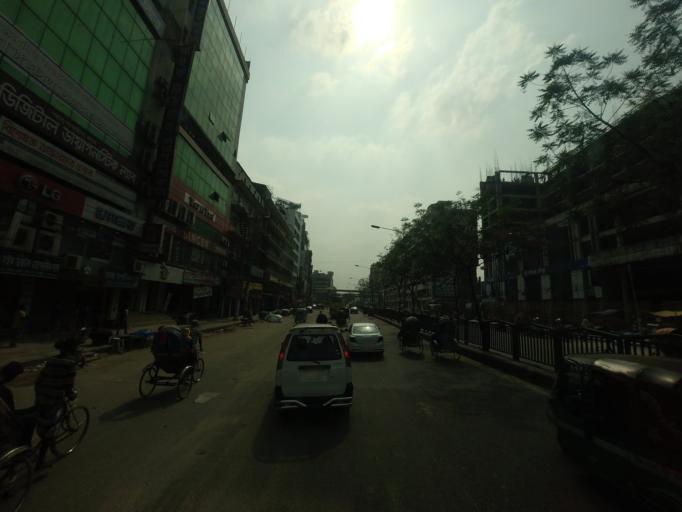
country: BD
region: Dhaka
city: Azimpur
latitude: 23.7994
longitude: 90.3547
